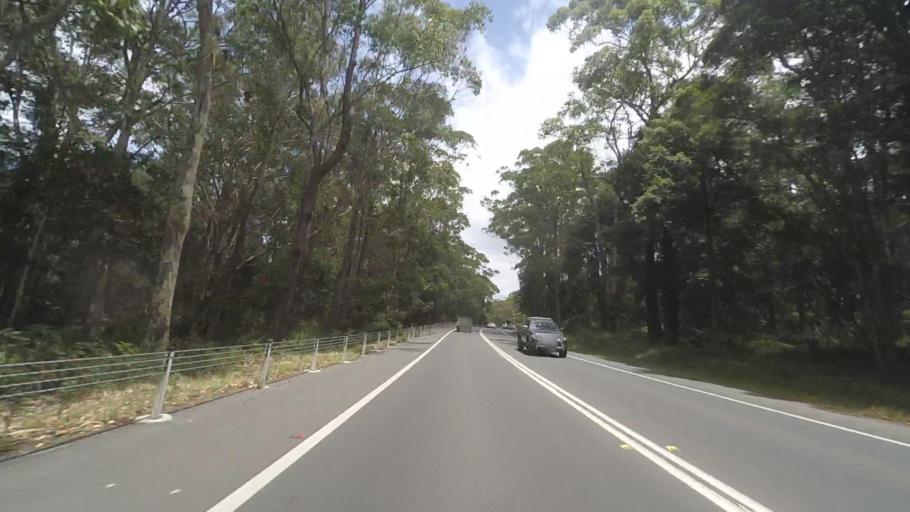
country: AU
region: New South Wales
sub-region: Shoalhaven Shire
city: Falls Creek
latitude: -35.0847
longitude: 150.5409
